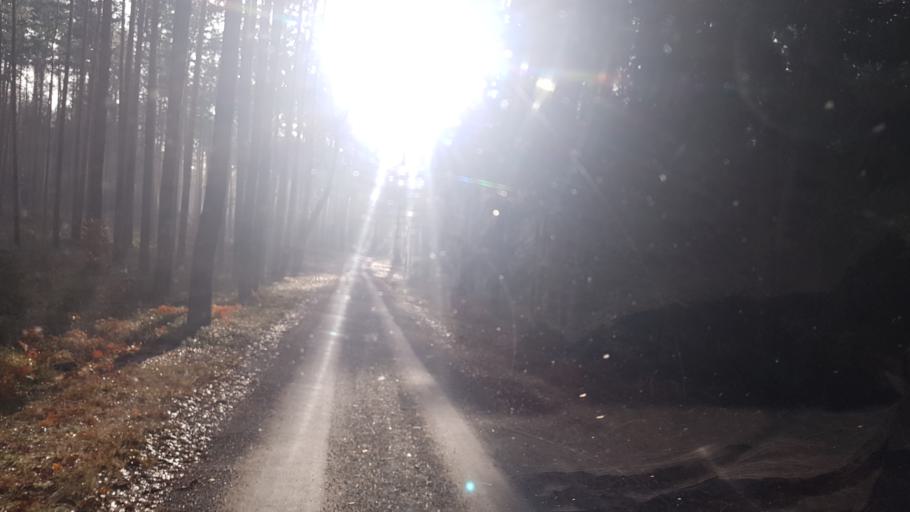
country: DE
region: Brandenburg
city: Schonborn
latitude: 51.6262
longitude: 13.5083
